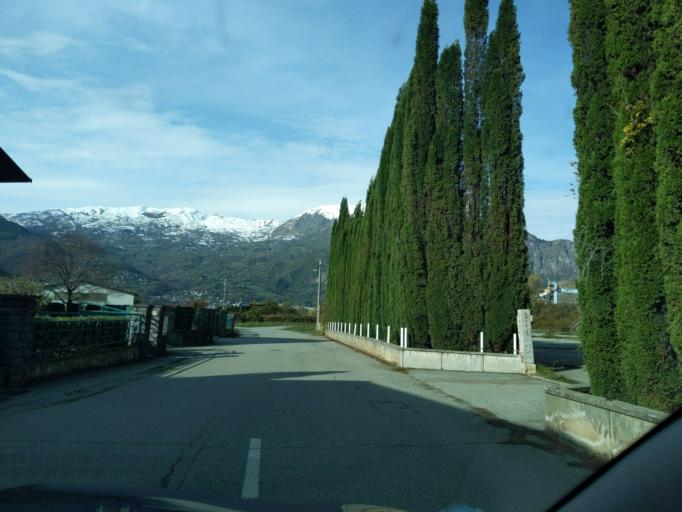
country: FR
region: Rhone-Alpes
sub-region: Departement de la Savoie
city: Villargondran
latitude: 45.2652
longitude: 6.3789
